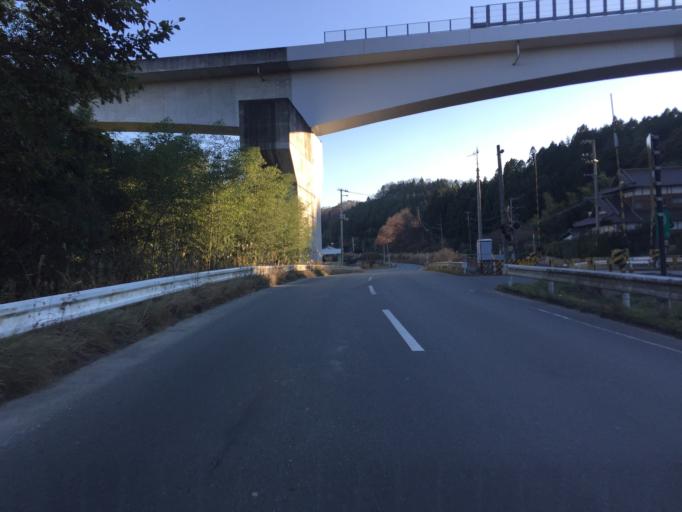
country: JP
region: Fukushima
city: Iwaki
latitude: 37.0970
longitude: 140.8599
